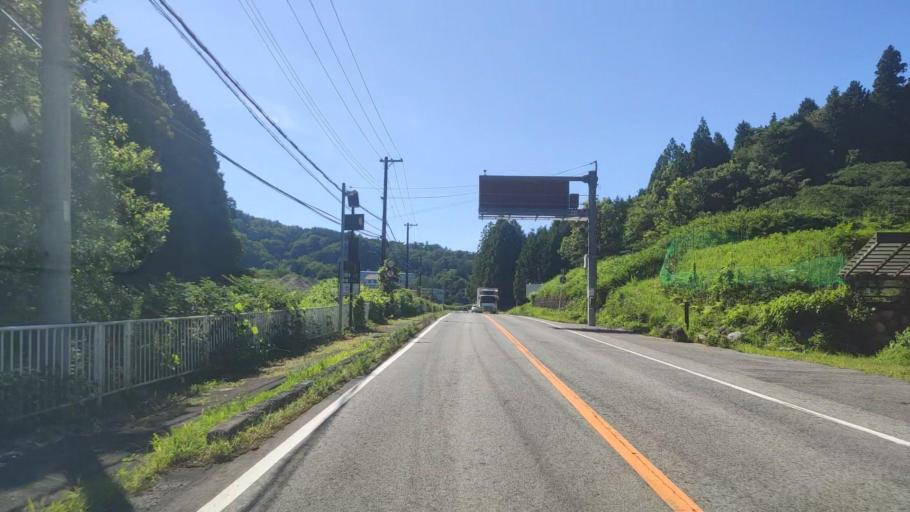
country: JP
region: Nara
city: Haibara-akanedai
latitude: 34.5859
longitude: 135.9669
